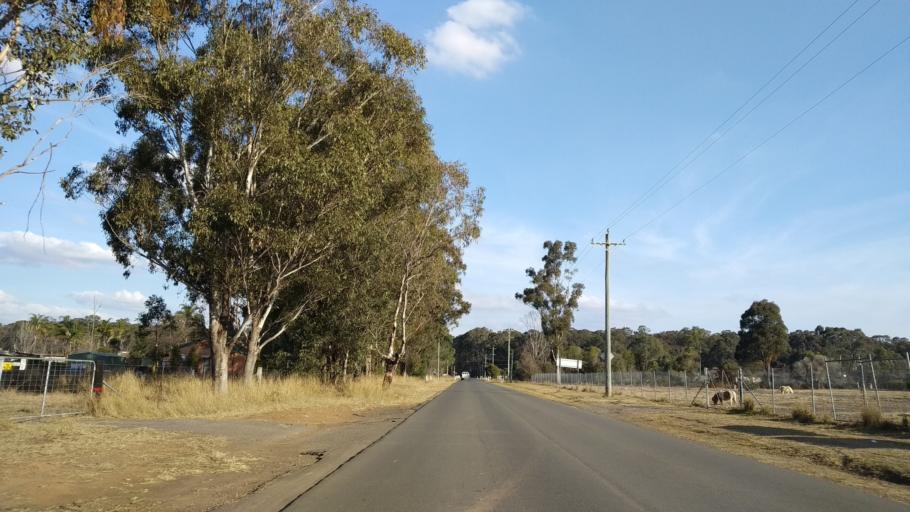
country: AU
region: New South Wales
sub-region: Penrith Municipality
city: Werrington County
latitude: -33.7134
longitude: 150.7560
